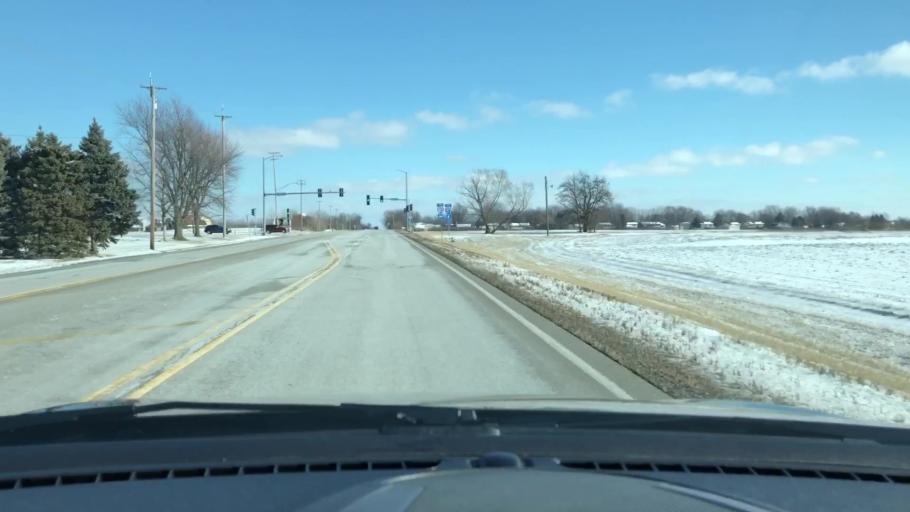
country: US
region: Illinois
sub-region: Will County
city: New Lenox
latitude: 41.4824
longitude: -88.0050
